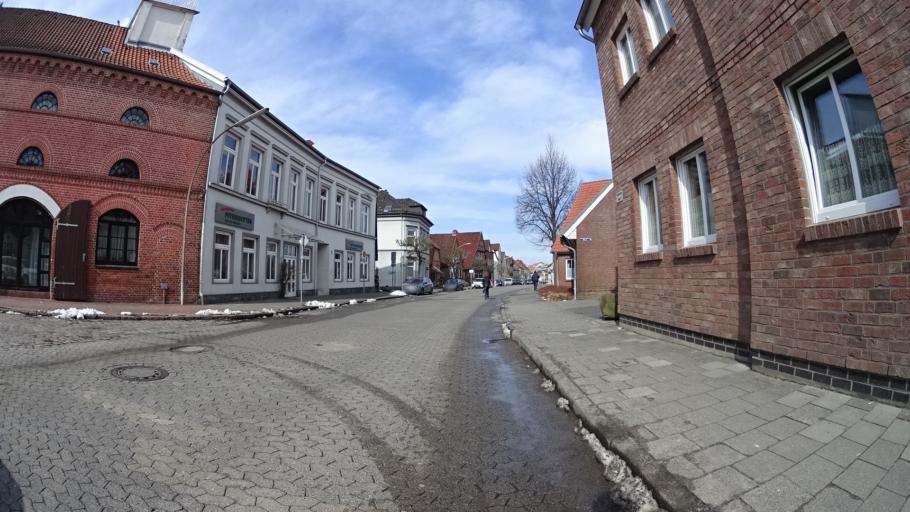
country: DE
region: Schleswig-Holstein
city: Preetz
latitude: 54.2309
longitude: 10.2803
